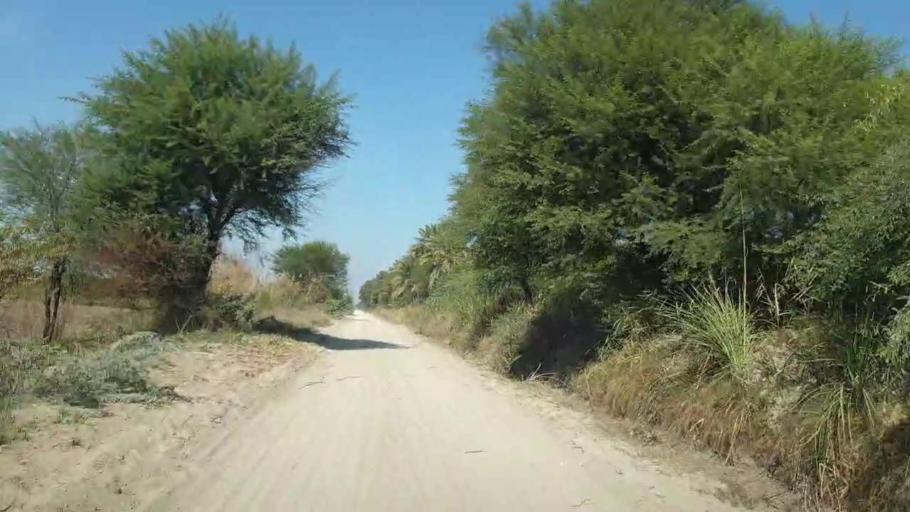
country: PK
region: Sindh
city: Mirpur Khas
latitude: 25.6505
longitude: 69.0274
